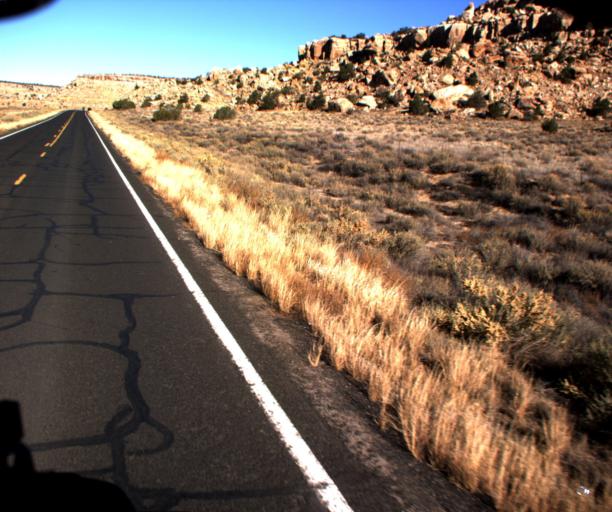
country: US
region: Arizona
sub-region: Navajo County
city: First Mesa
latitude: 35.8312
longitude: -110.2256
